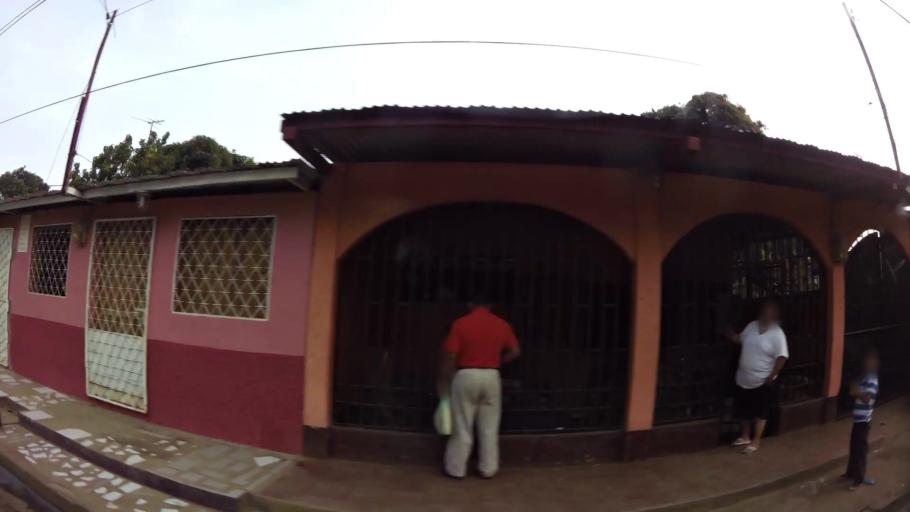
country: NI
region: Masaya
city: Masaya
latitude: 11.9835
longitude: -86.1013
